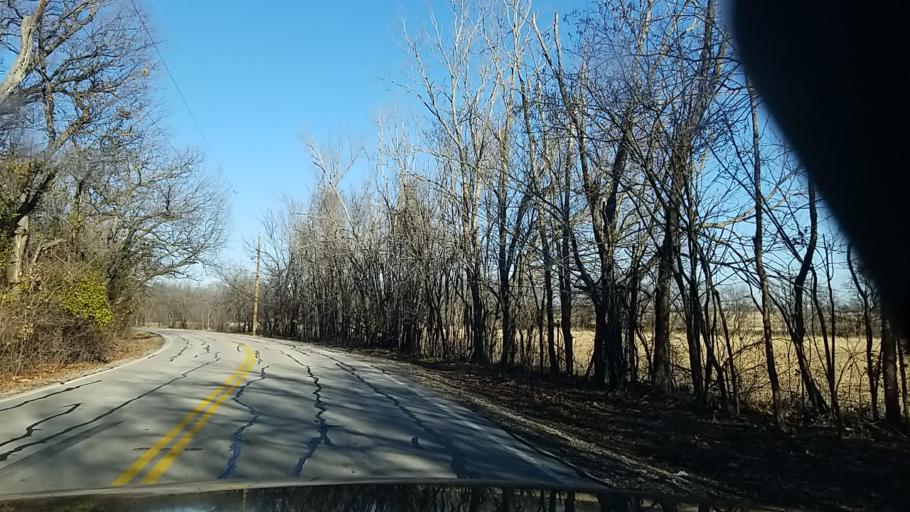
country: US
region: Texas
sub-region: Denton County
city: Argyle
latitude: 33.1503
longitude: -97.1400
